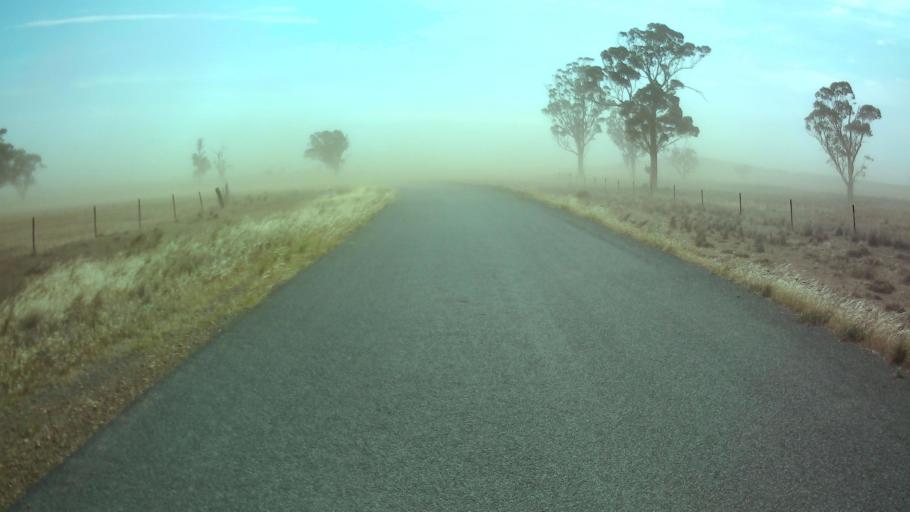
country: AU
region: New South Wales
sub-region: Weddin
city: Grenfell
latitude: -33.7365
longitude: 147.9957
